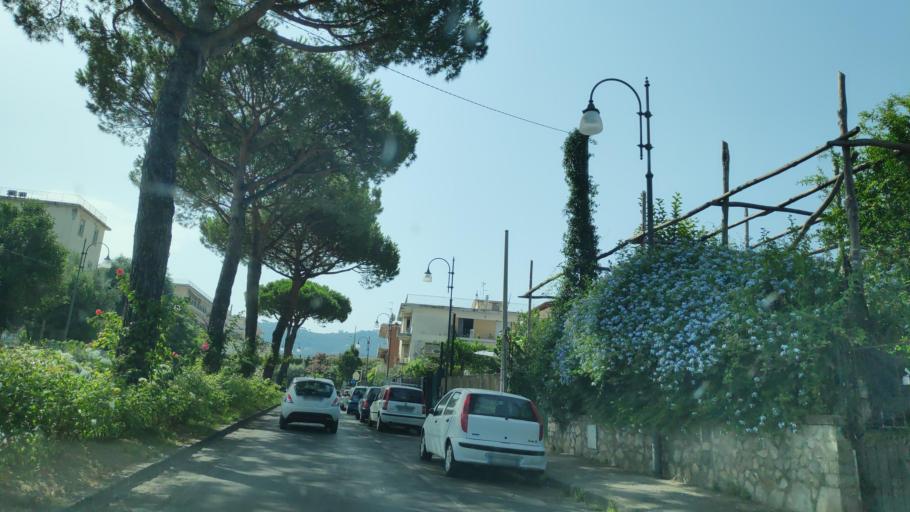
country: IT
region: Campania
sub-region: Provincia di Napoli
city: Sant'Agnello
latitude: 40.6325
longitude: 14.3976
